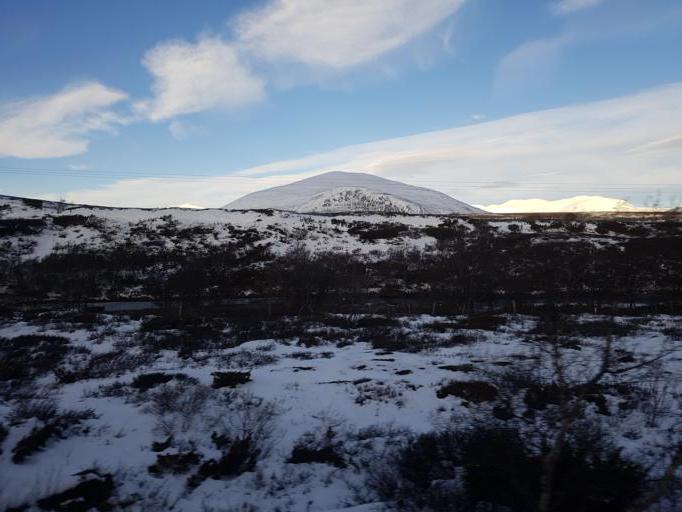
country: NO
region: Sor-Trondelag
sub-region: Oppdal
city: Oppdal
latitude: 62.2693
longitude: 9.5817
